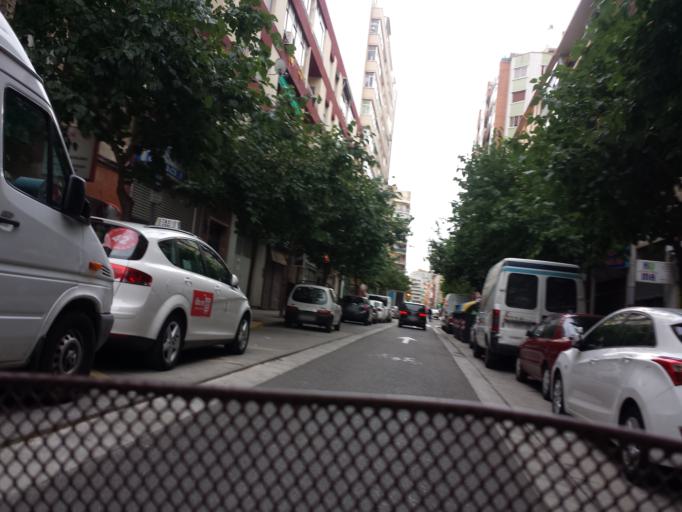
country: ES
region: Aragon
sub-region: Provincia de Zaragoza
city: Delicias
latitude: 41.6504
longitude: -0.8998
